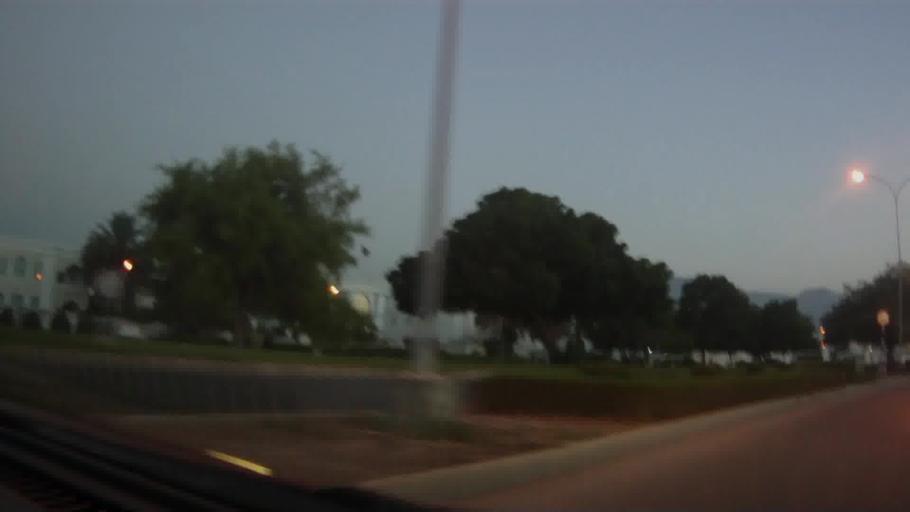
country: OM
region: Muhafazat Masqat
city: Bawshar
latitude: 23.6044
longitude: 58.4421
